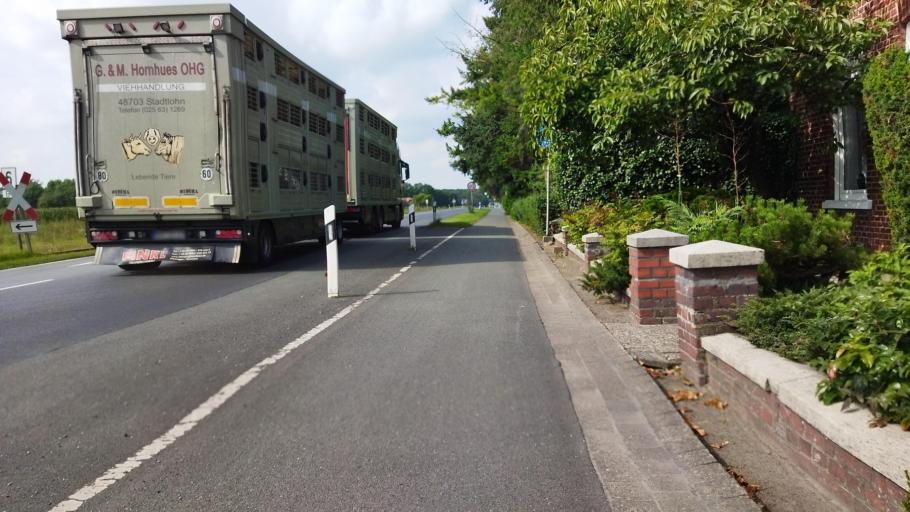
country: DE
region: North Rhine-Westphalia
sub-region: Regierungsbezirk Munster
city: Everswinkel
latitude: 51.9661
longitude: 7.8663
